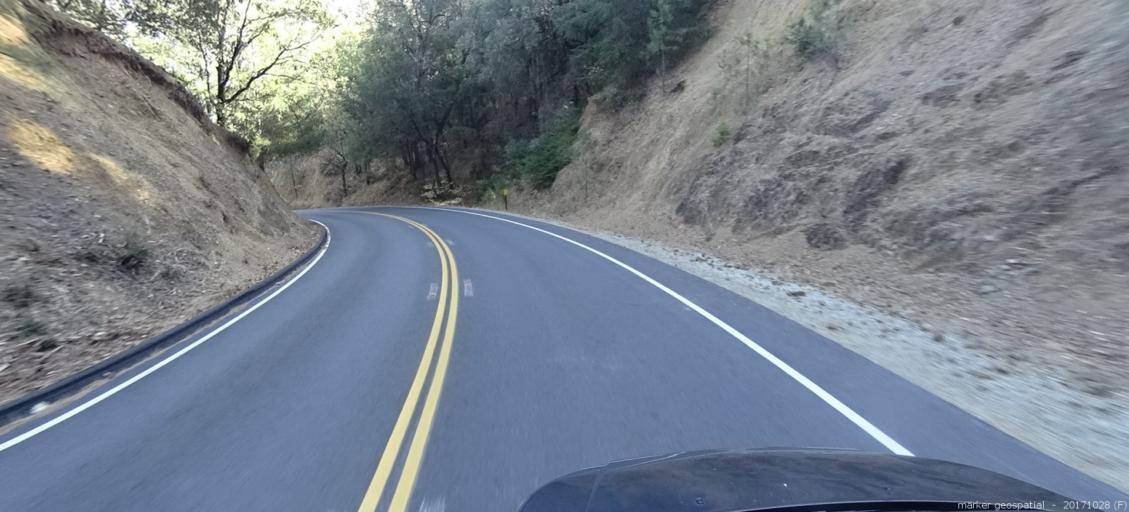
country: US
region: California
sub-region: Shasta County
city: Shasta
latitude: 40.6044
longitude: -122.5569
